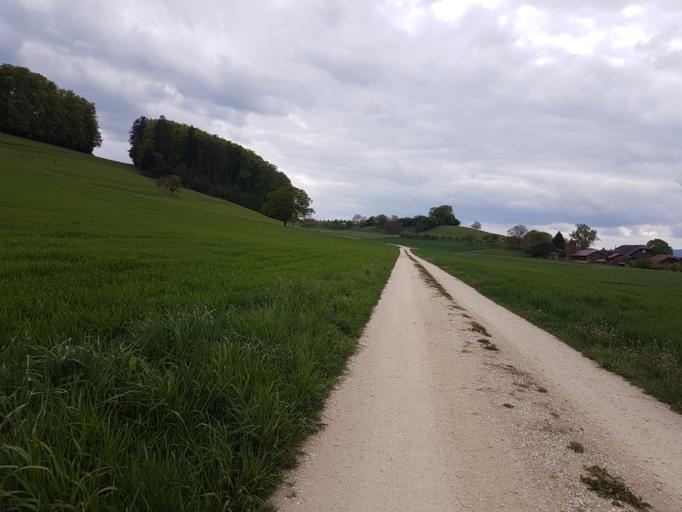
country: CH
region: Bern
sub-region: Seeland District
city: Leuzigen
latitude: 47.1805
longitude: 7.4826
